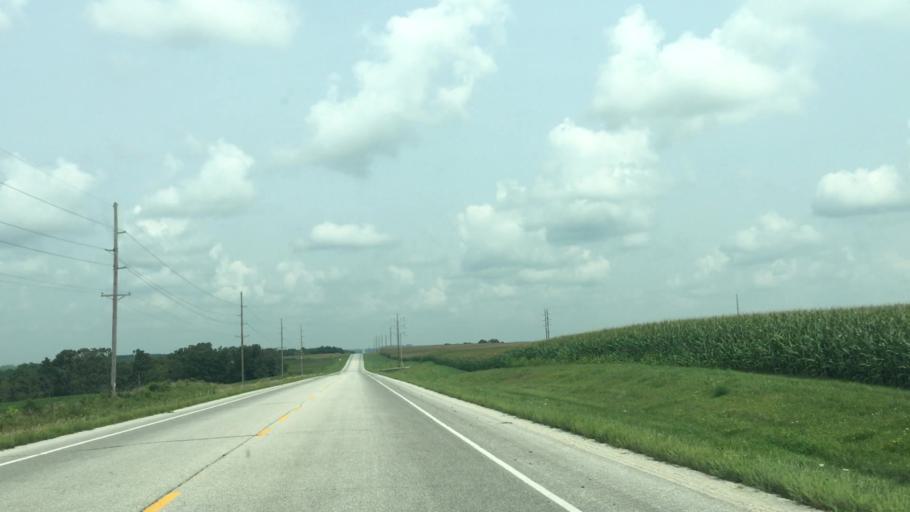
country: US
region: Minnesota
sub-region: Fillmore County
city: Harmony
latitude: 43.5628
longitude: -91.9297
